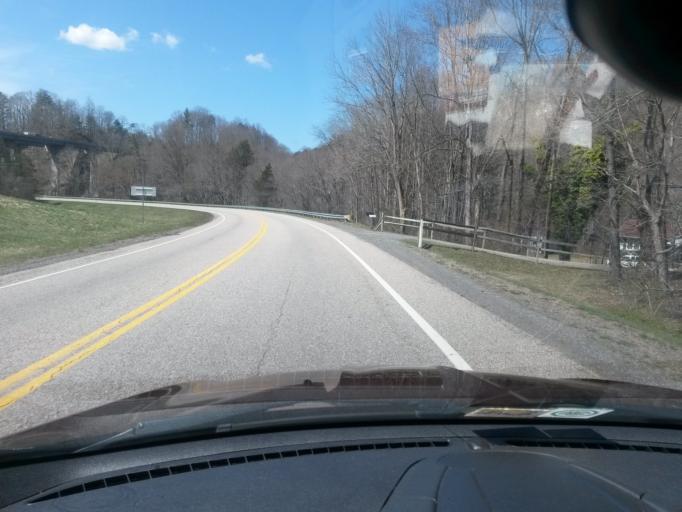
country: US
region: Virginia
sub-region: City of Covington
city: Covington
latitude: 37.8091
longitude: -80.0587
